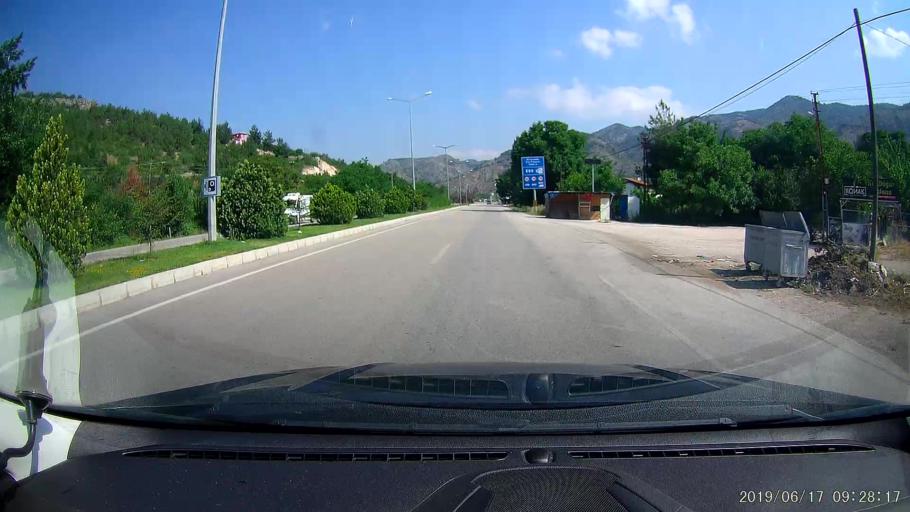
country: TR
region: Amasya
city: Amasya
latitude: 40.6866
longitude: 35.8227
